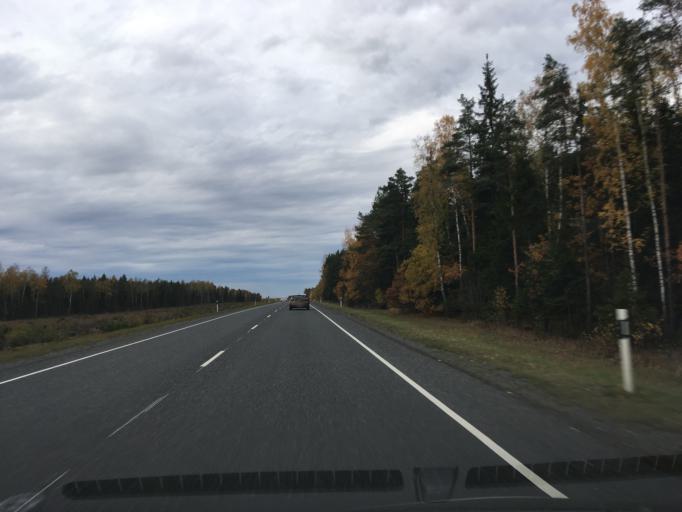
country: EE
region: Harju
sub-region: Nissi vald
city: Turba
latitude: 58.9562
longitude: 24.0776
